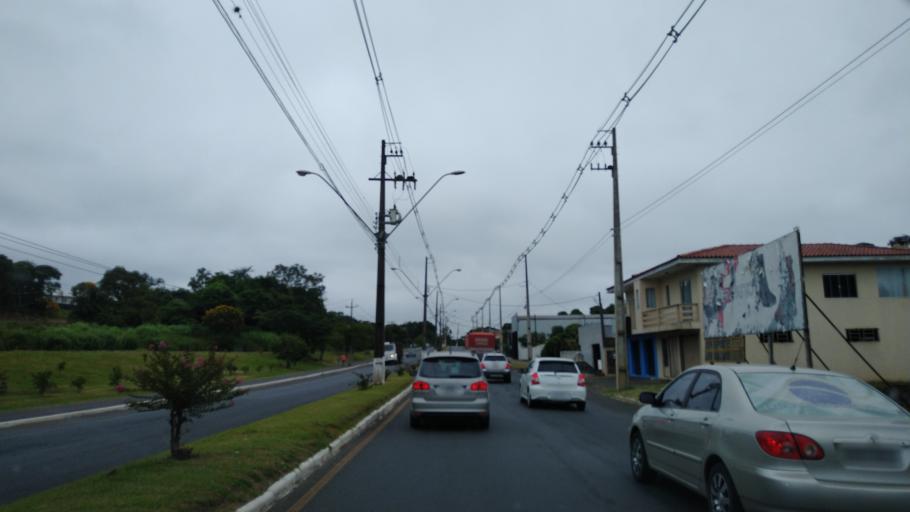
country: BR
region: Santa Catarina
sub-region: Porto Uniao
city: Porto Uniao
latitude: -26.2550
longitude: -51.0767
